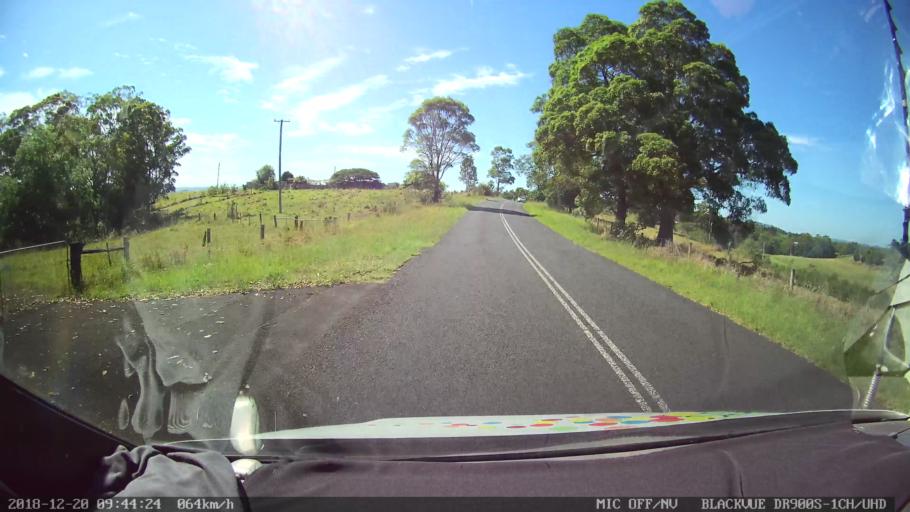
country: AU
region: New South Wales
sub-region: Lismore Municipality
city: Lismore
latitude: -28.7343
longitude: 153.2986
